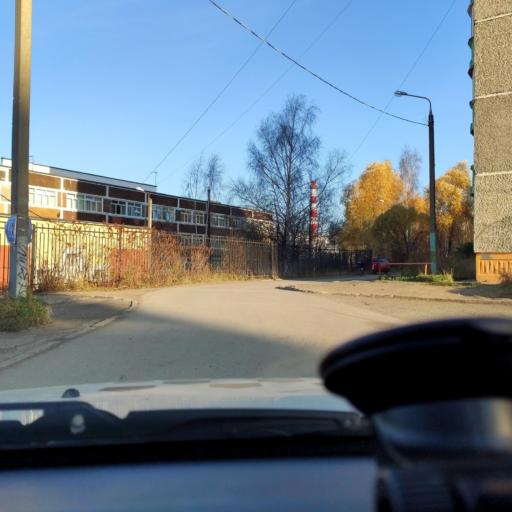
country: RU
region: Perm
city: Perm
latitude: 58.0560
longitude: 56.3513
